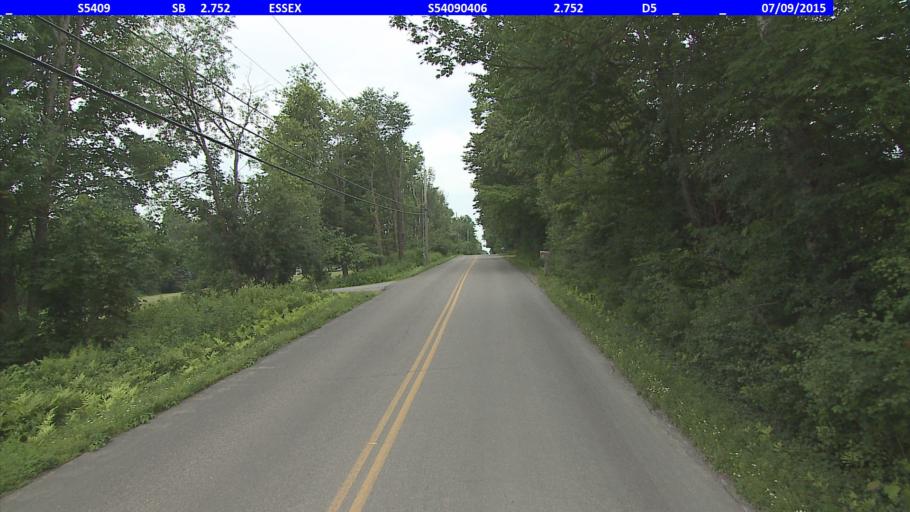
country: US
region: Vermont
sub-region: Chittenden County
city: Essex Junction
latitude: 44.5482
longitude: -73.0707
